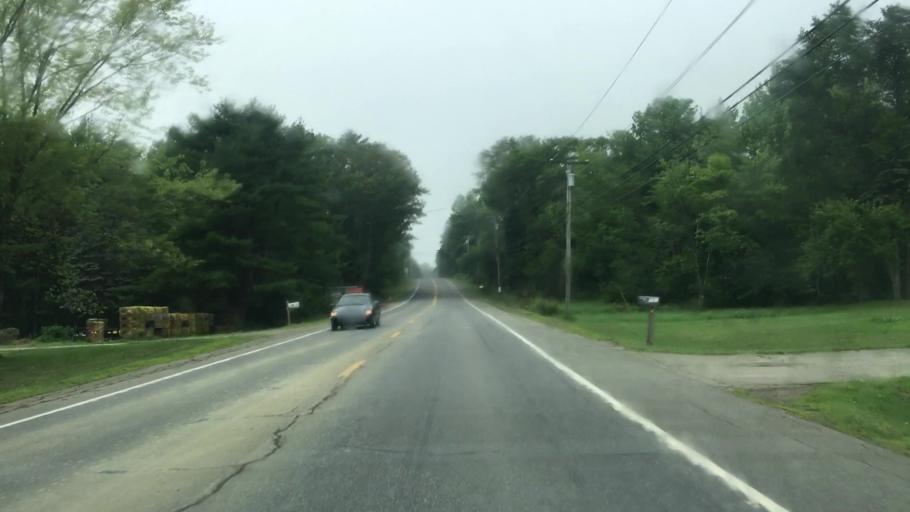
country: US
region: Maine
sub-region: Lincoln County
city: Wiscasset
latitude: 44.0559
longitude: -69.6845
